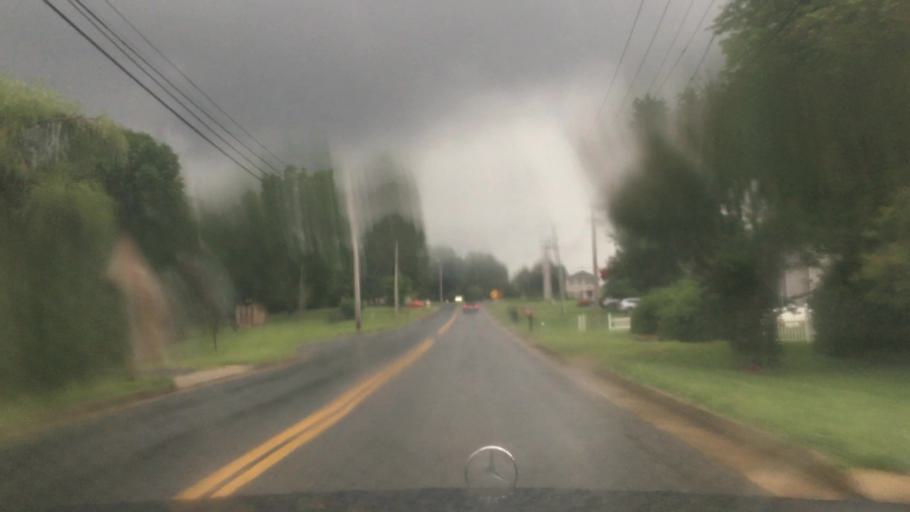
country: US
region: Virginia
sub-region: Campbell County
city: Timberlake
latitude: 37.3681
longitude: -79.2265
